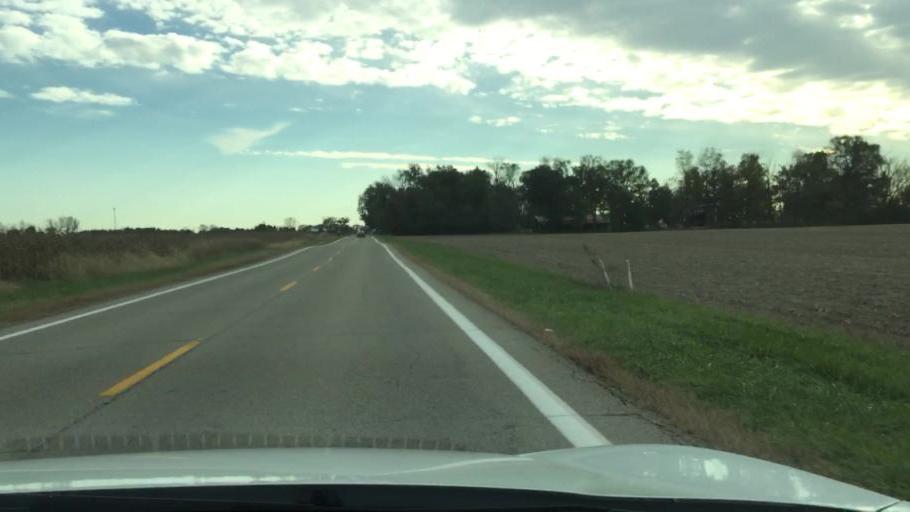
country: US
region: Ohio
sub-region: Champaign County
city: Mechanicsburg
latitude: 40.1075
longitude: -83.5396
